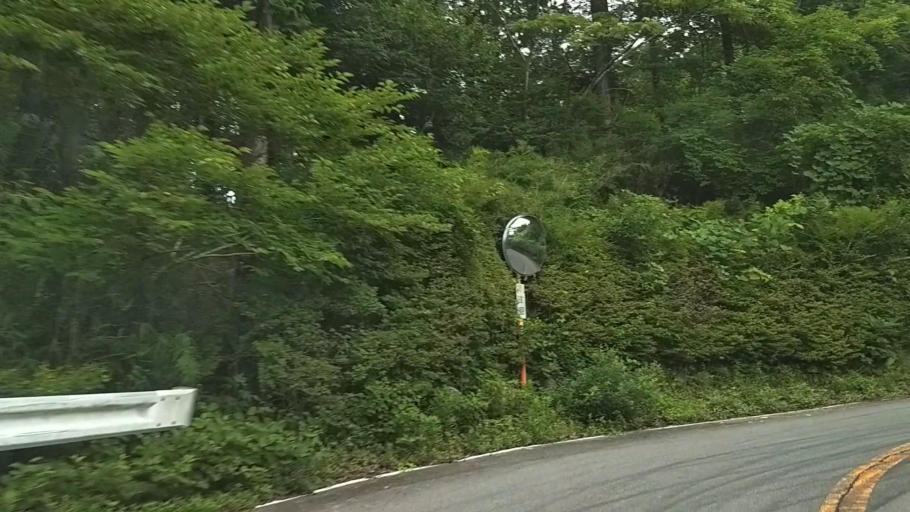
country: JP
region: Shizuoka
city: Gotemba
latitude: 35.3188
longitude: 139.0186
